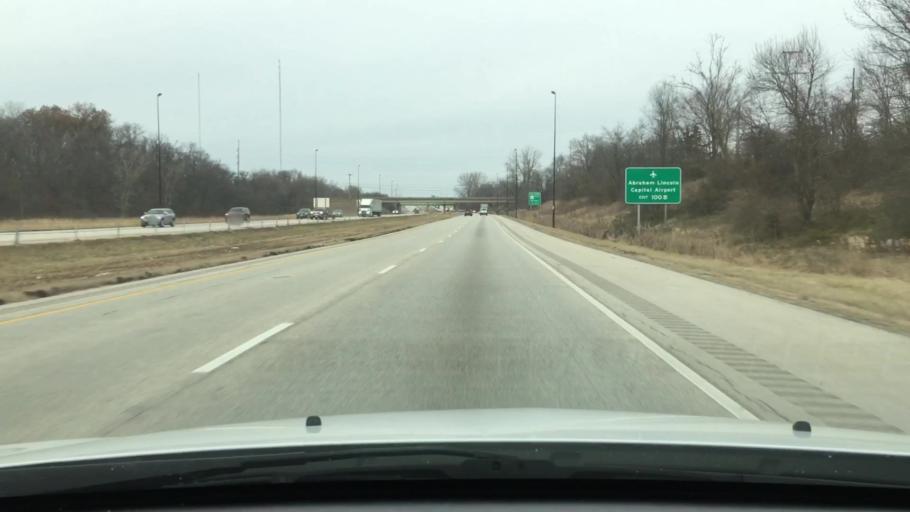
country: US
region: Illinois
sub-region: Sangamon County
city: Grandview
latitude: 39.8205
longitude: -89.5926
